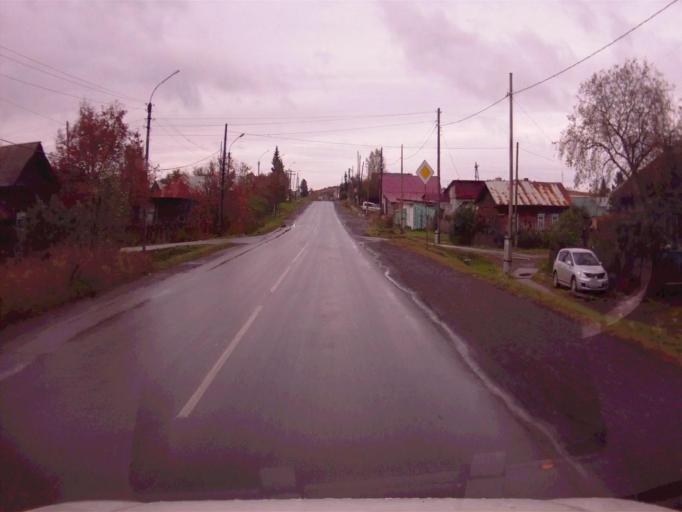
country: RU
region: Chelyabinsk
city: Verkhniy Ufaley
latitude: 56.0540
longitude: 60.2044
